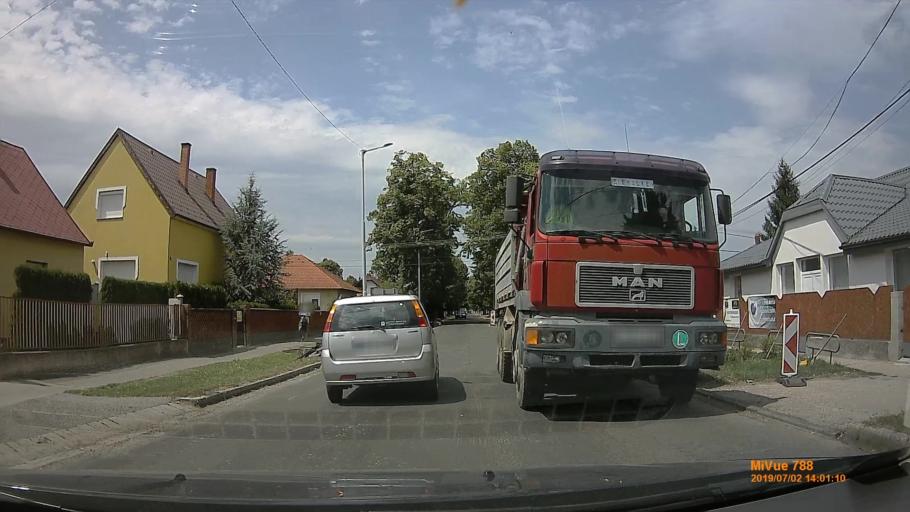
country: HU
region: Gyor-Moson-Sopron
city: Mosonmagyarovar
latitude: 47.8720
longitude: 17.2765
